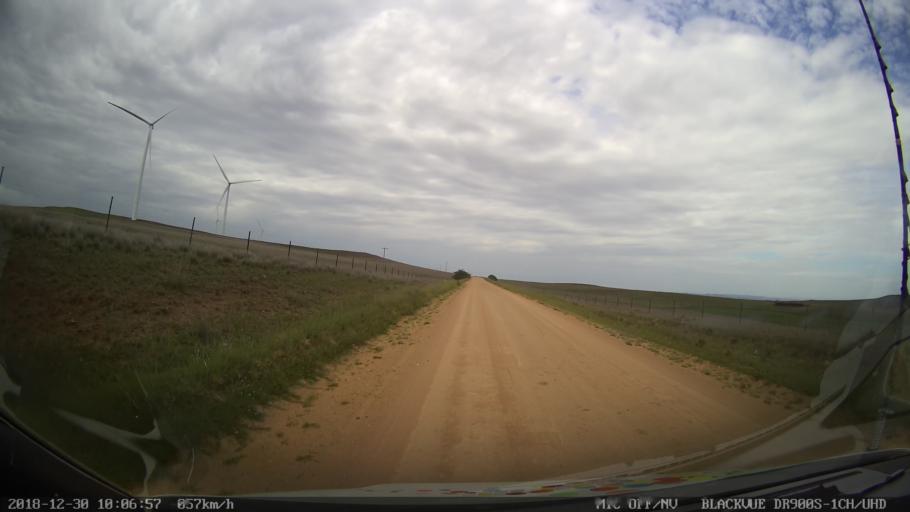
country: AU
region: New South Wales
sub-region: Cooma-Monaro
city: Cooma
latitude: -36.5360
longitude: 149.1262
